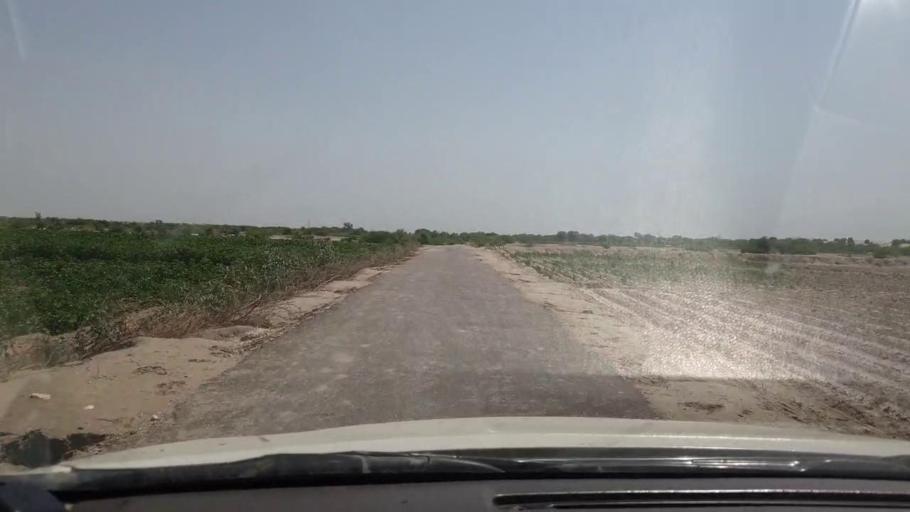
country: PK
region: Sindh
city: Rohri
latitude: 27.5193
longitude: 69.0883
